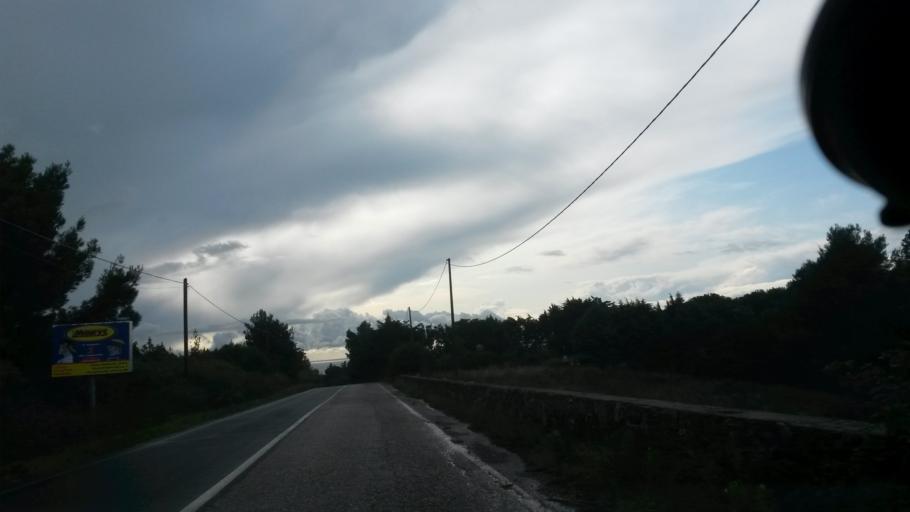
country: IT
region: Tuscany
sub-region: Provincia di Livorno
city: Rosignano Marittimo
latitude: 43.4161
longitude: 10.4529
